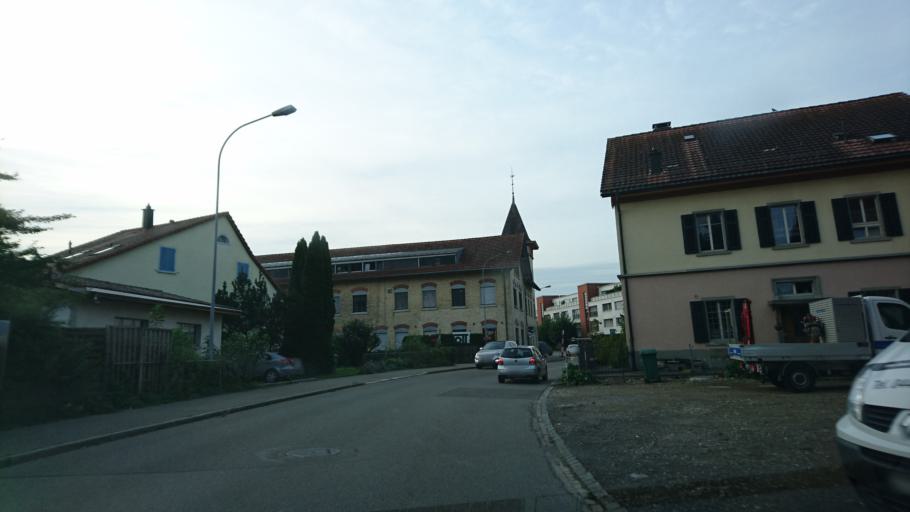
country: CH
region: Zurich
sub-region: Bezirk Uster
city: Uster / Nieder-Uster
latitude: 47.3467
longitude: 8.6966
